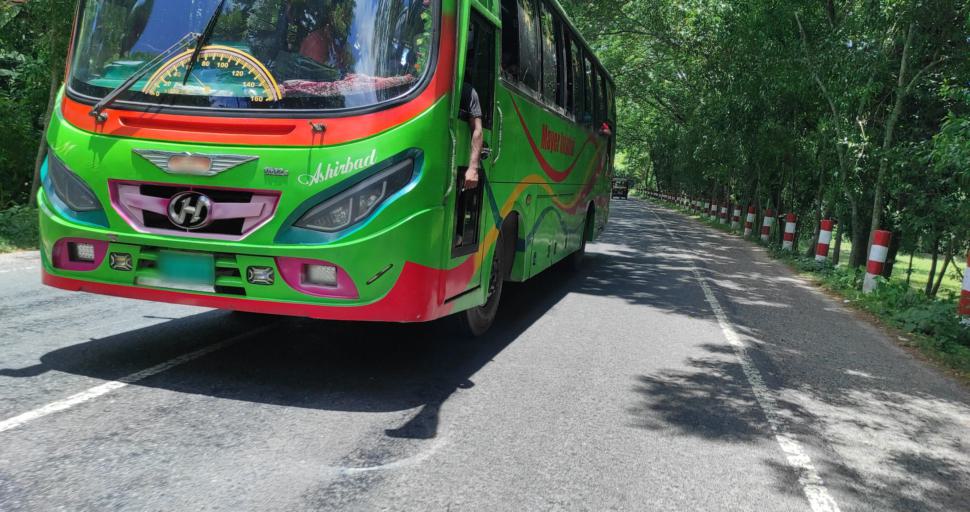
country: BD
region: Barisal
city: Gaurnadi
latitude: 22.8416
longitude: 90.2513
